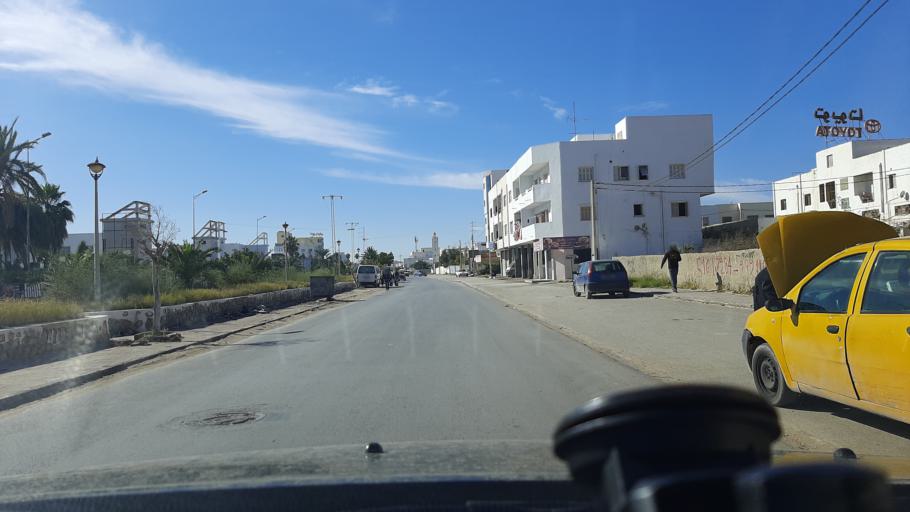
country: TN
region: Safaqis
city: Sfax
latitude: 34.7237
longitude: 10.7369
